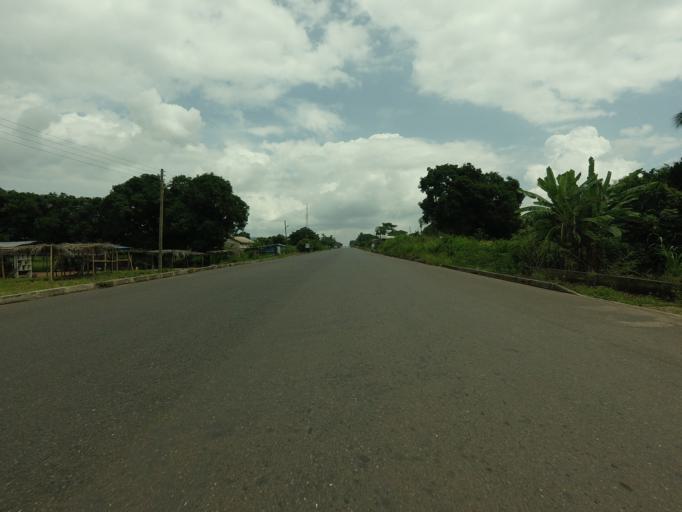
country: GH
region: Volta
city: Ho
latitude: 6.5359
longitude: 0.2315
